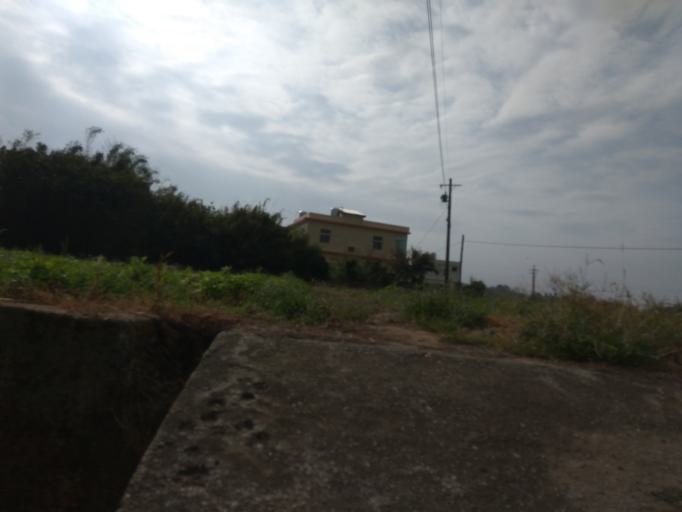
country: TW
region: Taiwan
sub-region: Hsinchu
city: Zhubei
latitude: 24.9812
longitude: 121.0293
